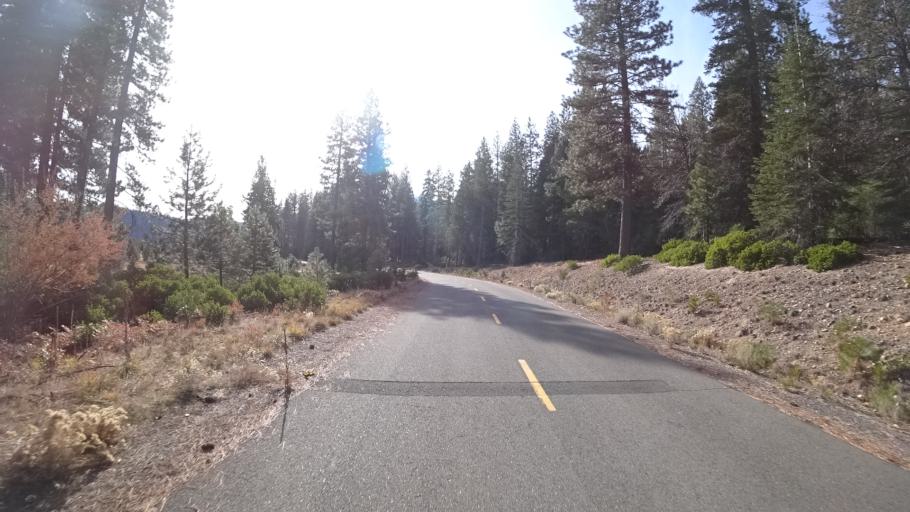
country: US
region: California
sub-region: Siskiyou County
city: Weed
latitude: 41.4008
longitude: -122.3887
